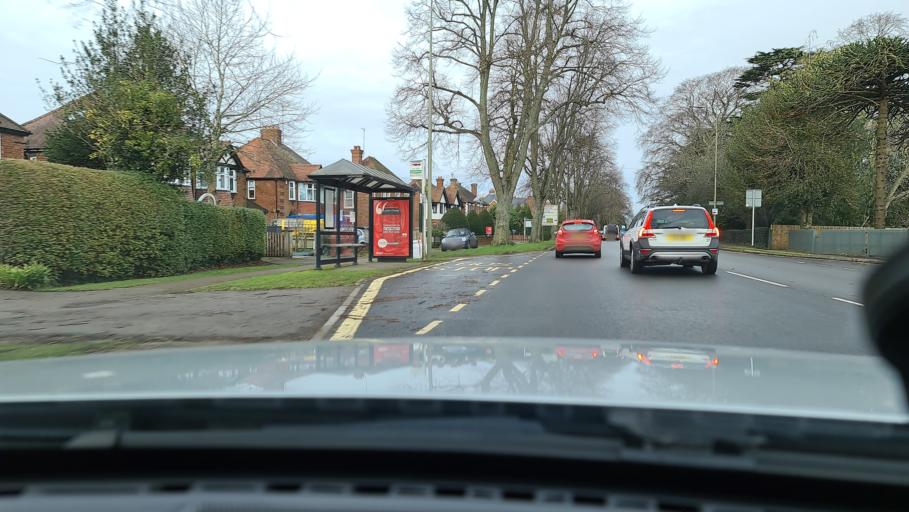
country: GB
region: England
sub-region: Oxfordshire
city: Banbury
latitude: 52.0532
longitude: -1.3381
